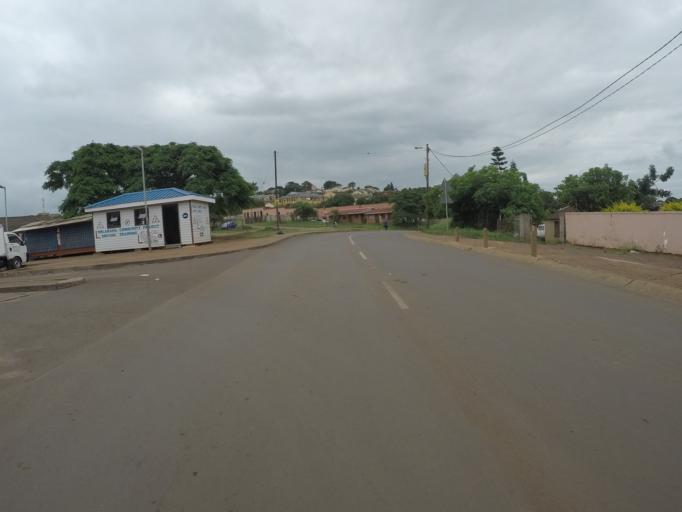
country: ZA
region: KwaZulu-Natal
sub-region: uThungulu District Municipality
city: Empangeni
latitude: -28.7733
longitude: 31.8633
